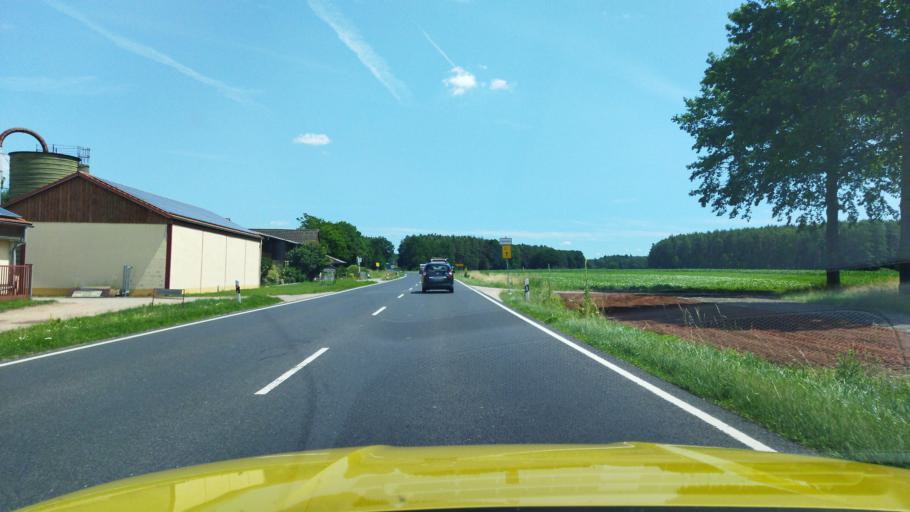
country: DE
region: Bavaria
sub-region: Regierungsbezirk Mittelfranken
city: Allersberg
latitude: 49.2518
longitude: 11.1795
